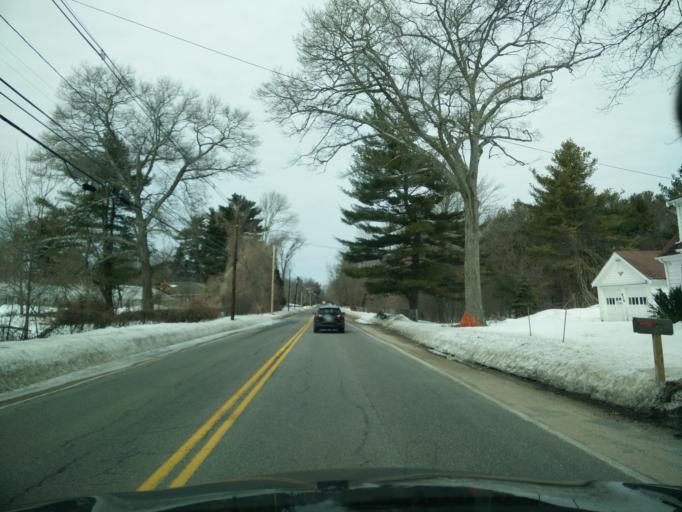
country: US
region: Massachusetts
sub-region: Norfolk County
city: Walpole
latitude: 42.1781
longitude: -71.2436
